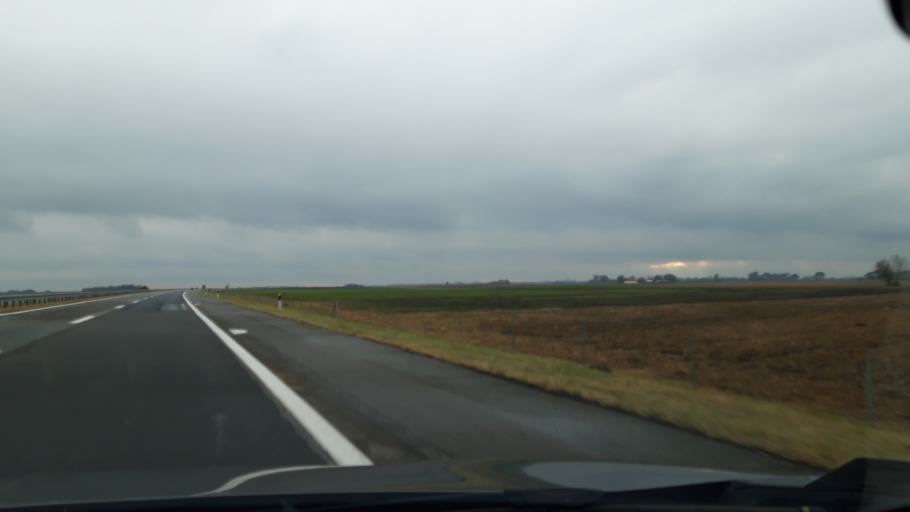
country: RS
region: Autonomna Pokrajina Vojvodina
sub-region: Severnobacki Okrug
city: Backa Topola
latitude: 45.8656
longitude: 19.6996
